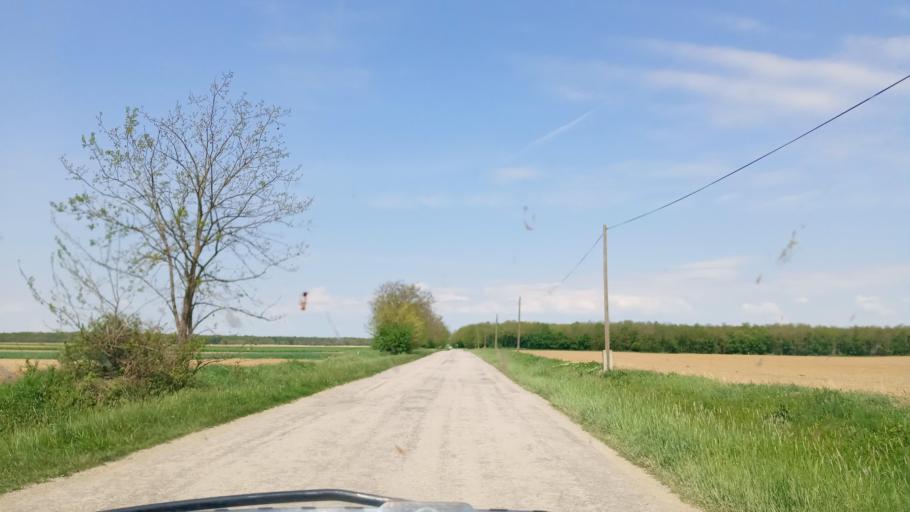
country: HU
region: Baranya
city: Boly
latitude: 45.8788
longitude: 18.5758
